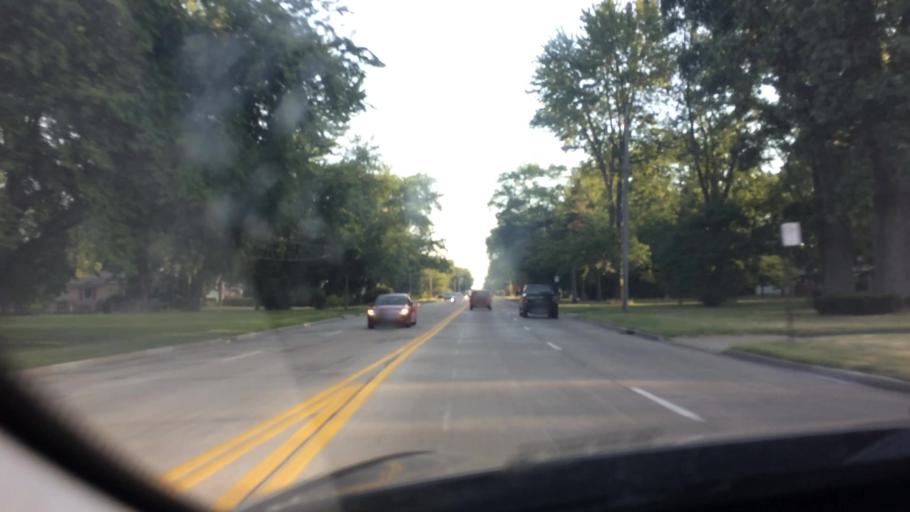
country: US
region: Ohio
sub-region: Lucas County
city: Ottawa Hills
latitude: 41.6784
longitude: -83.6441
